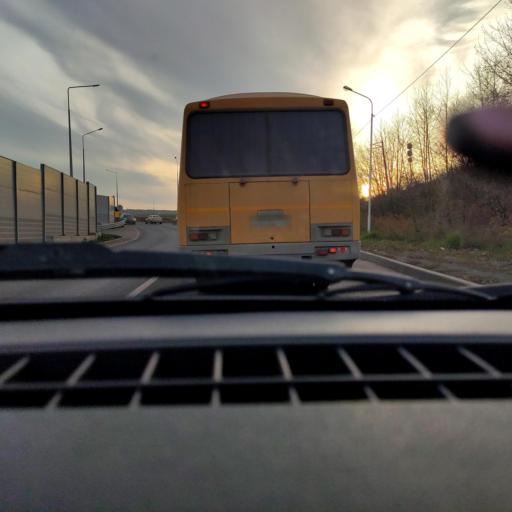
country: RU
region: Bashkortostan
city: Ufa
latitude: 54.8301
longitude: 56.1310
